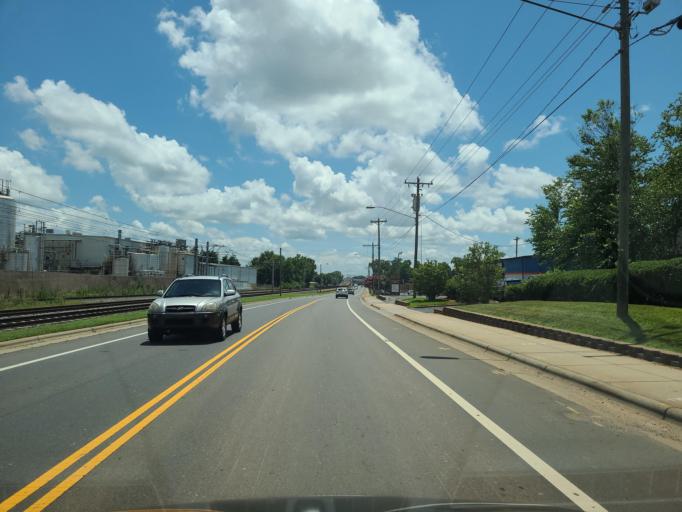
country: US
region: North Carolina
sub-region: Mecklenburg County
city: Charlotte
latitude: 35.1711
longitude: -80.8782
